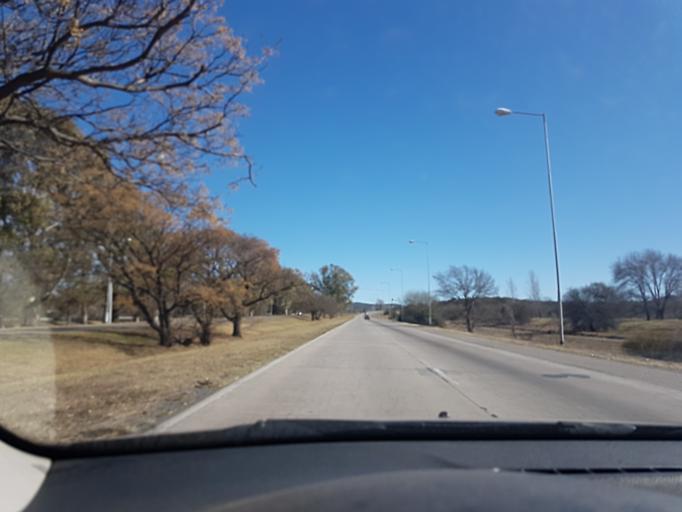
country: AR
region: Cordoba
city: Villa Carlos Paz
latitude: -31.4437
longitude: -64.4362
